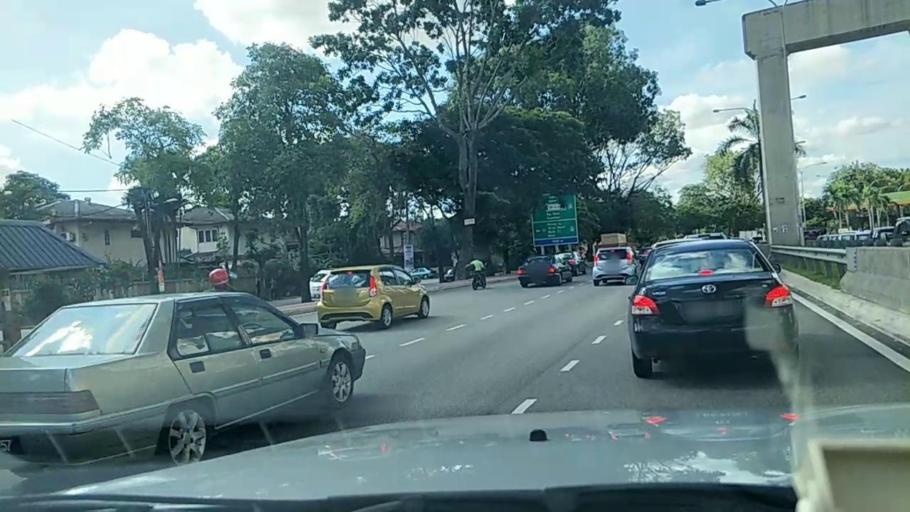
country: MY
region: Selangor
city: Subang Jaya
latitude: 3.0579
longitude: 101.5919
